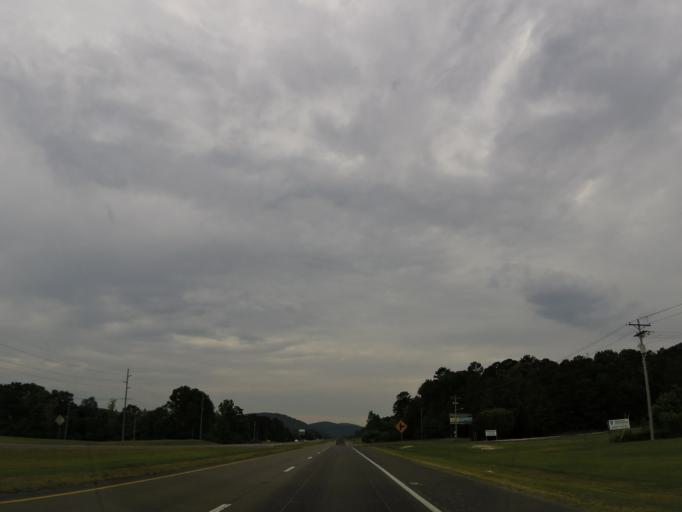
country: US
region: Alabama
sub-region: Jackson County
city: Scottsboro
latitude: 34.6245
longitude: -86.0798
